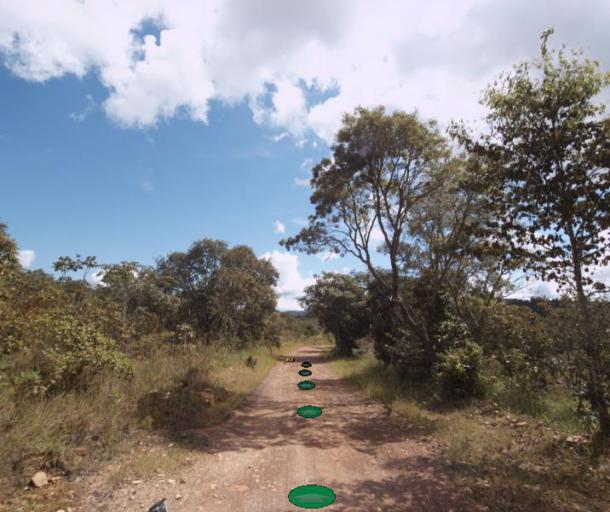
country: BR
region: Goias
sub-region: Pirenopolis
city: Pirenopolis
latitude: -15.7920
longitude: -48.9041
